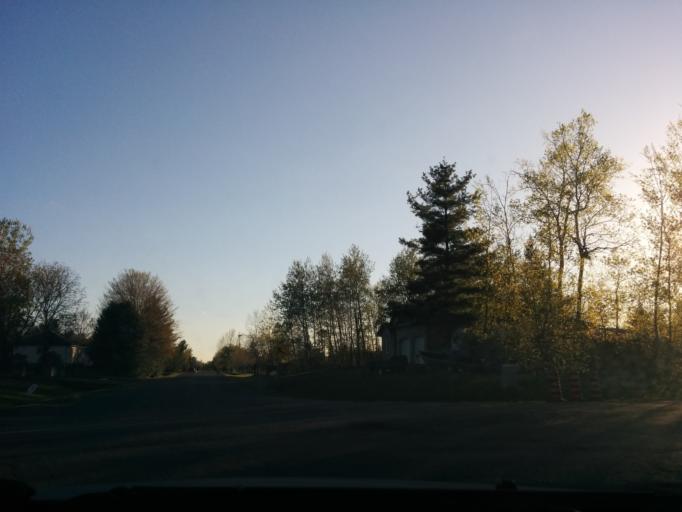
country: CA
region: Ontario
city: Ottawa
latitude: 45.1481
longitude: -75.5976
